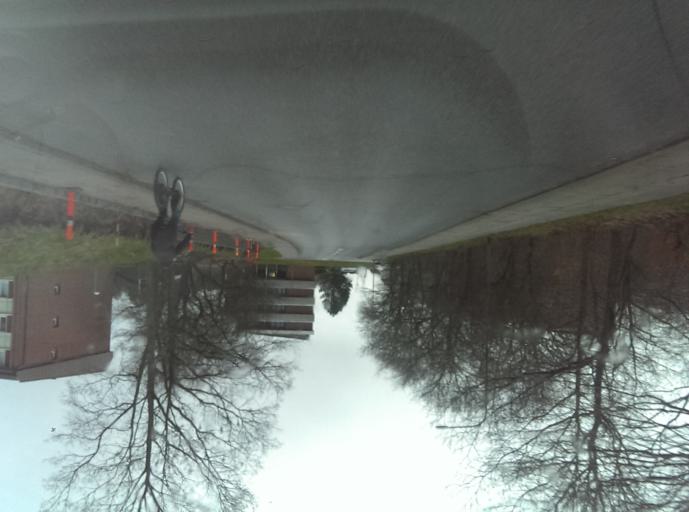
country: DK
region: South Denmark
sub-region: Esbjerg Kommune
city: Esbjerg
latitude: 55.4725
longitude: 8.4893
